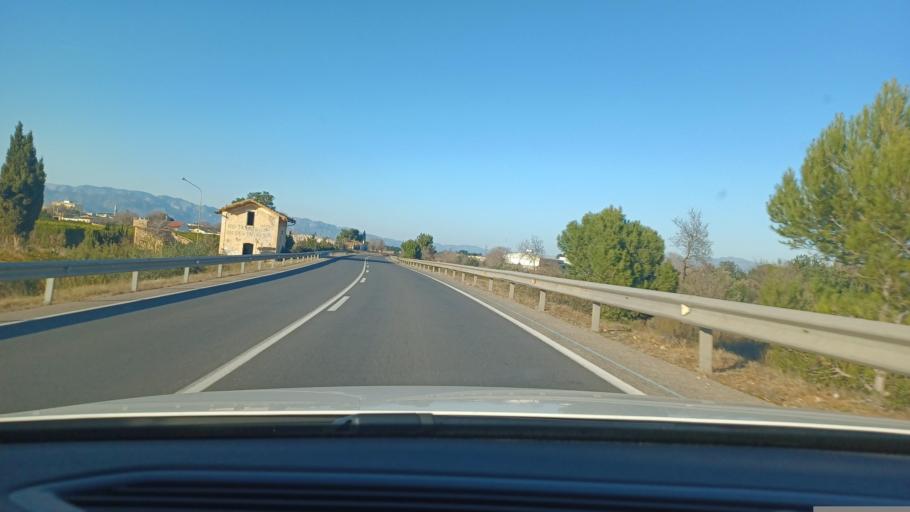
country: ES
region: Catalonia
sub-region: Provincia de Tarragona
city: Santa Barbara
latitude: 40.7117
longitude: 0.5069
